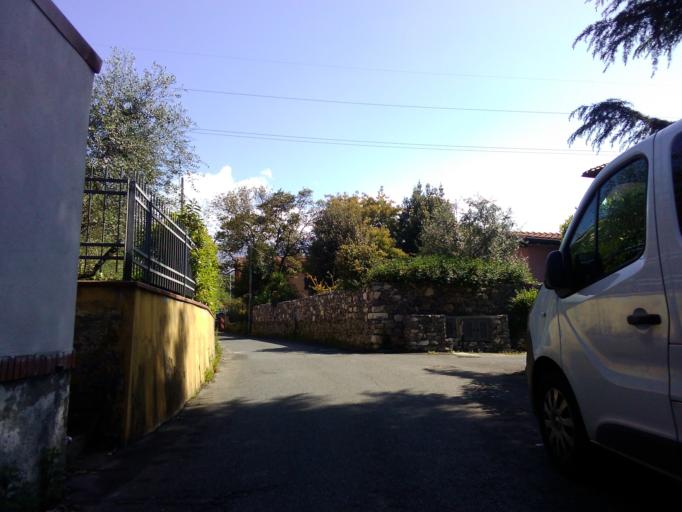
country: IT
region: Tuscany
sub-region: Provincia di Massa-Carrara
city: Carrara
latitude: 44.0623
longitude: 10.0675
